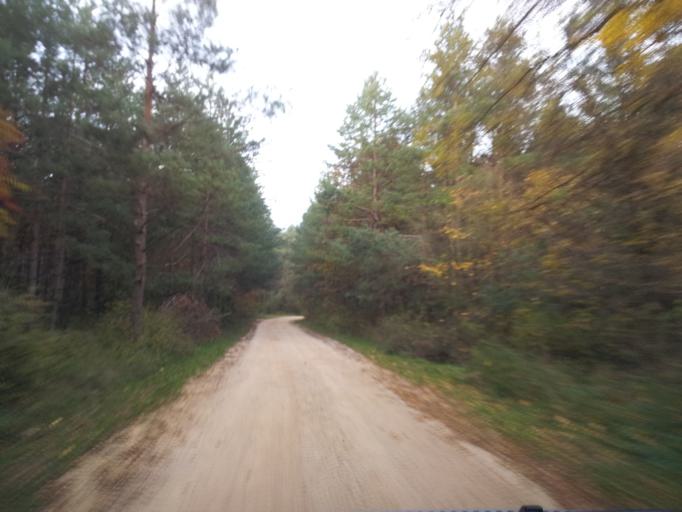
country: HU
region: Gyor-Moson-Sopron
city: Bakonyszentlaszlo
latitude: 47.3715
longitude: 17.8184
